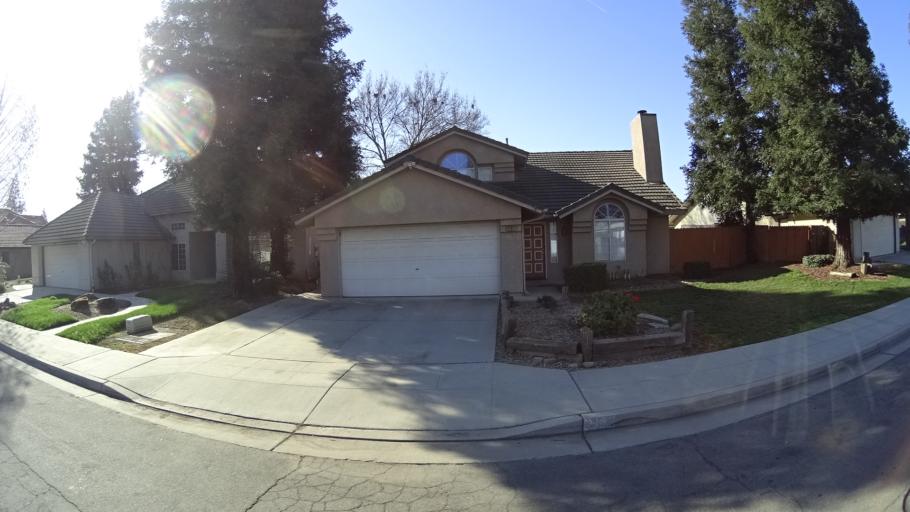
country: US
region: California
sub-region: Fresno County
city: Clovis
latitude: 36.8701
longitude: -119.7439
